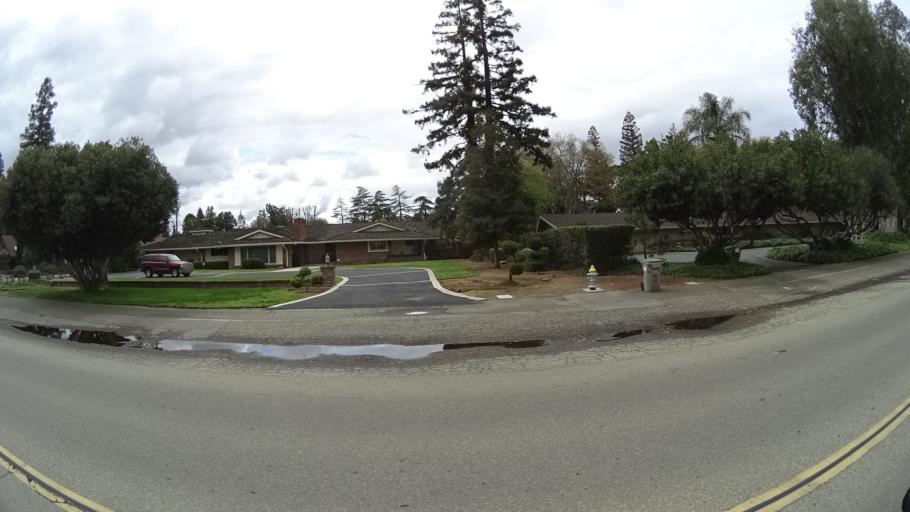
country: US
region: California
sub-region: Fresno County
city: Fresno
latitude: 36.8176
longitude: -119.8354
